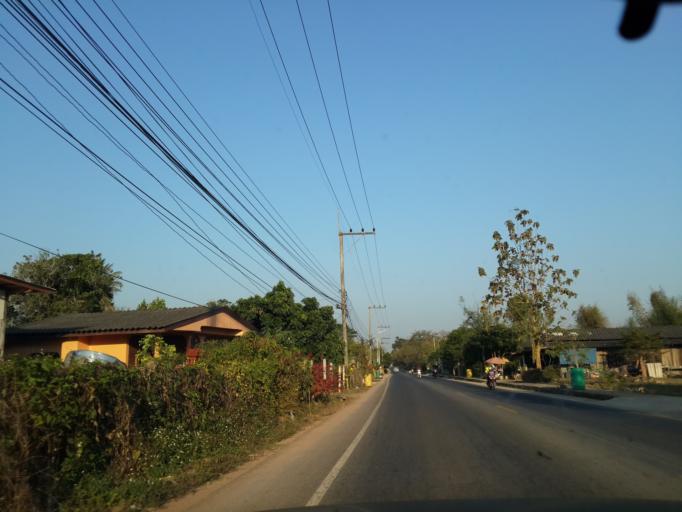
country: TH
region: Chiang Mai
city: Chai Prakan
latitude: 19.8014
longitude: 99.1577
